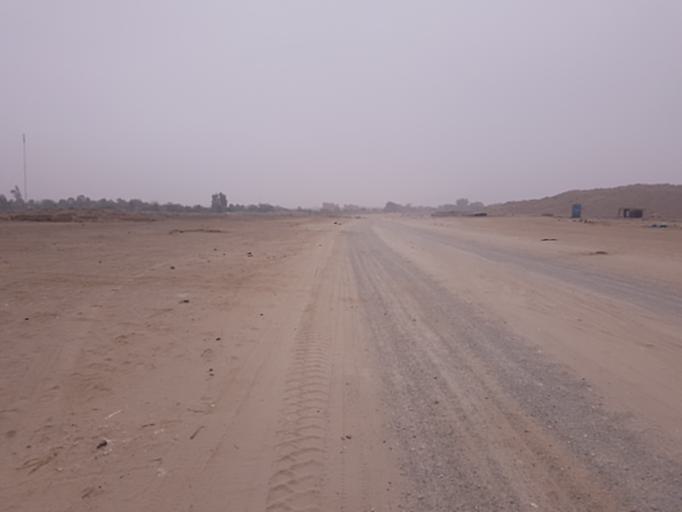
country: PE
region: Lima
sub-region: Lima
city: Santa Maria
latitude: -11.9841
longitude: -76.9102
